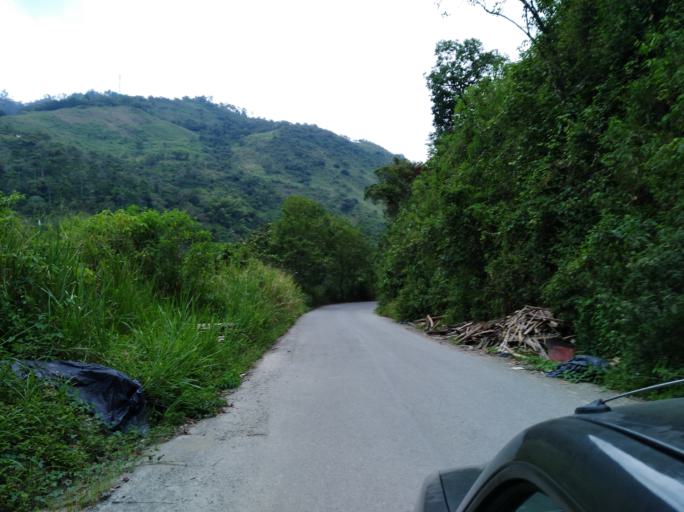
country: CO
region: Caldas
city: Salamina
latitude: 5.4103
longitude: -75.4744
